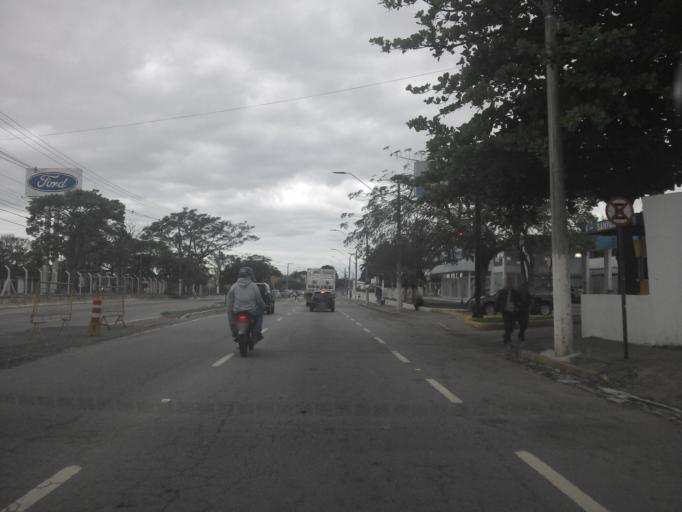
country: BR
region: Sao Paulo
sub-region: Taubate
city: Taubate
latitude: -23.0242
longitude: -45.5896
